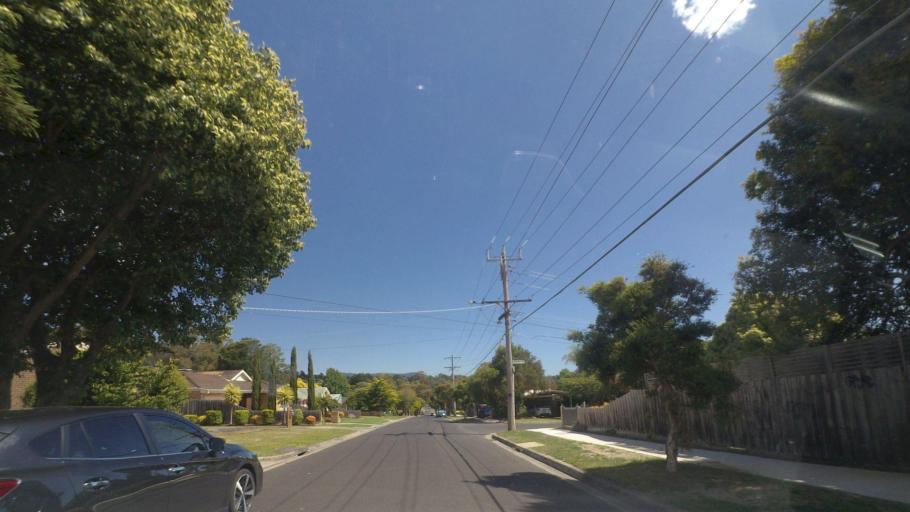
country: AU
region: Victoria
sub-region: Yarra Ranges
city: Kilsyth
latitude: -37.8013
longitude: 145.3302
